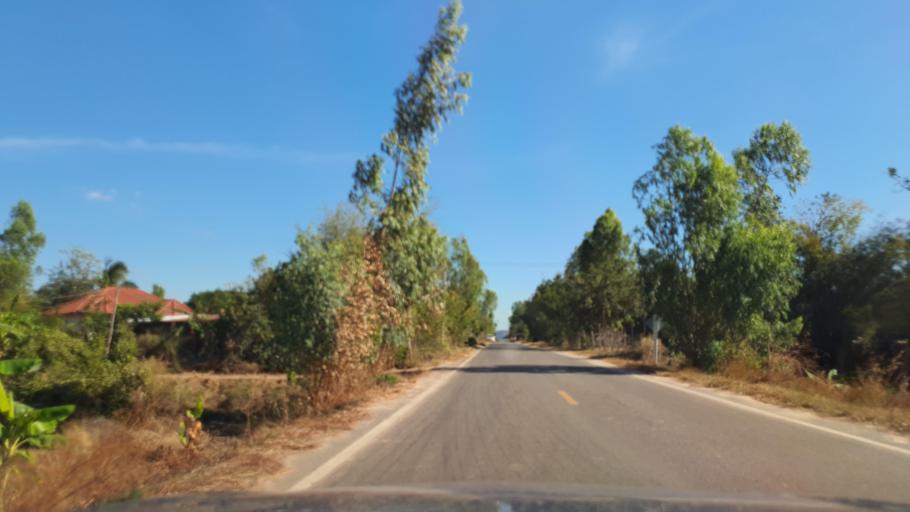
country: TH
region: Kalasin
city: Khao Wong
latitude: 16.7262
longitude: 104.1006
